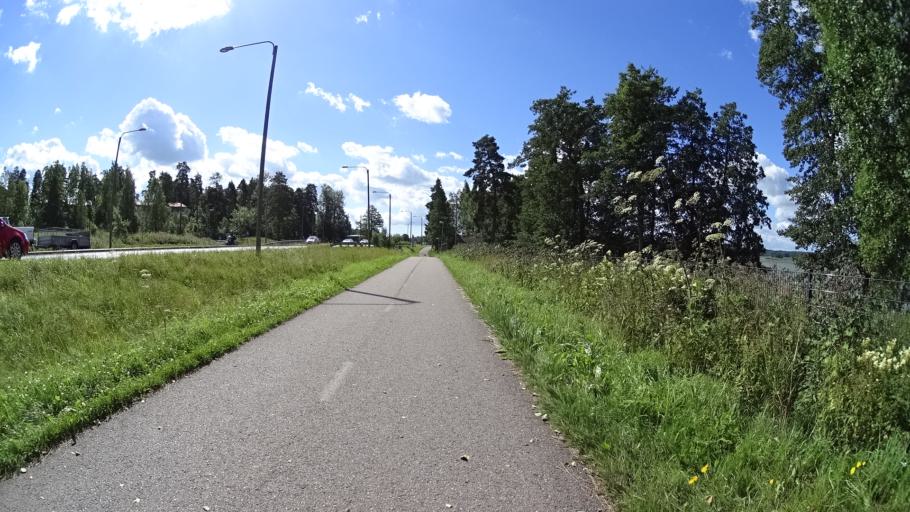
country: FI
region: Uusimaa
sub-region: Helsinki
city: Jaervenpaeae
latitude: 60.4474
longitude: 25.0778
